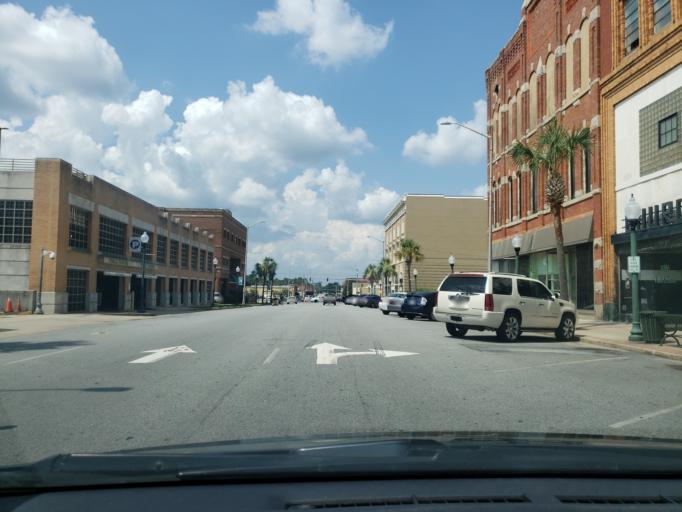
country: US
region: Georgia
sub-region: Dougherty County
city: Albany
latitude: 31.5772
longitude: -84.1514
